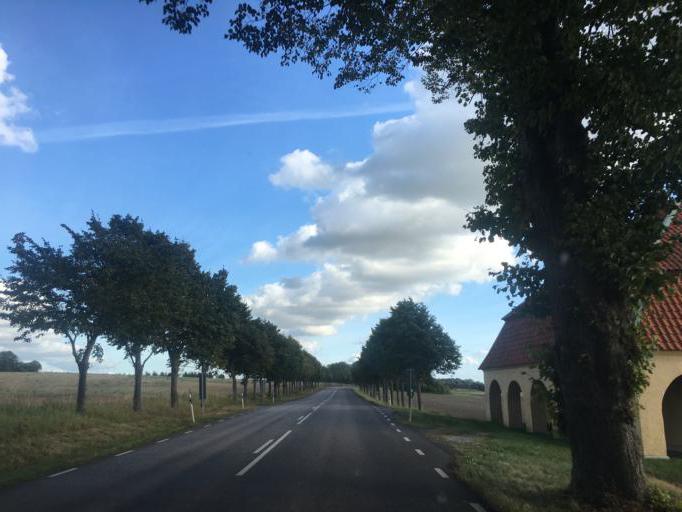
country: SE
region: Skane
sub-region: Eslovs Kommun
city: Eslov
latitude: 55.7774
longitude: 13.3018
